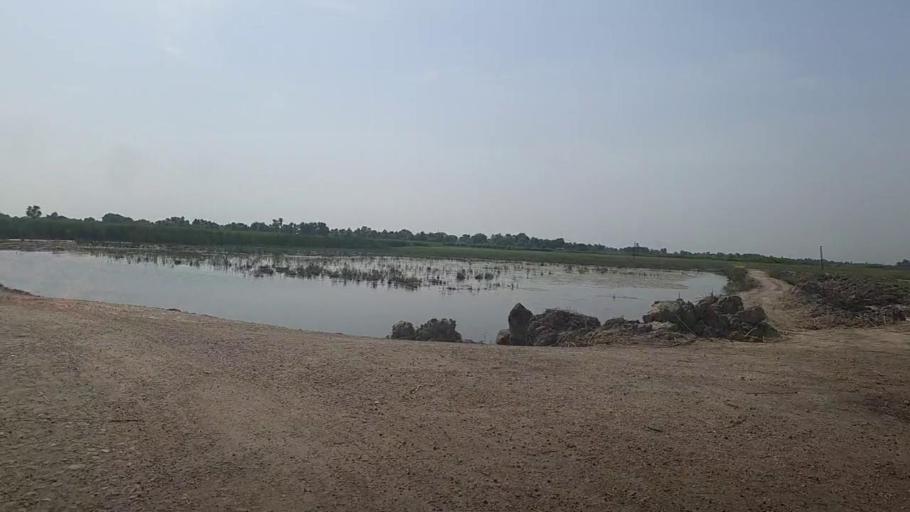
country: PK
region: Sindh
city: Ubauro
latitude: 28.1476
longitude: 69.8039
